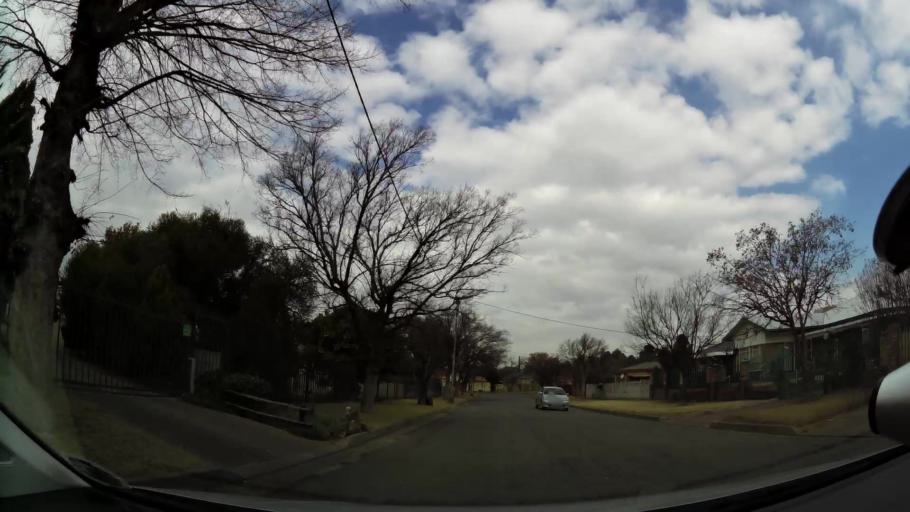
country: ZA
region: Orange Free State
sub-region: Fezile Dabi District Municipality
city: Kroonstad
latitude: -27.6477
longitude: 27.2377
